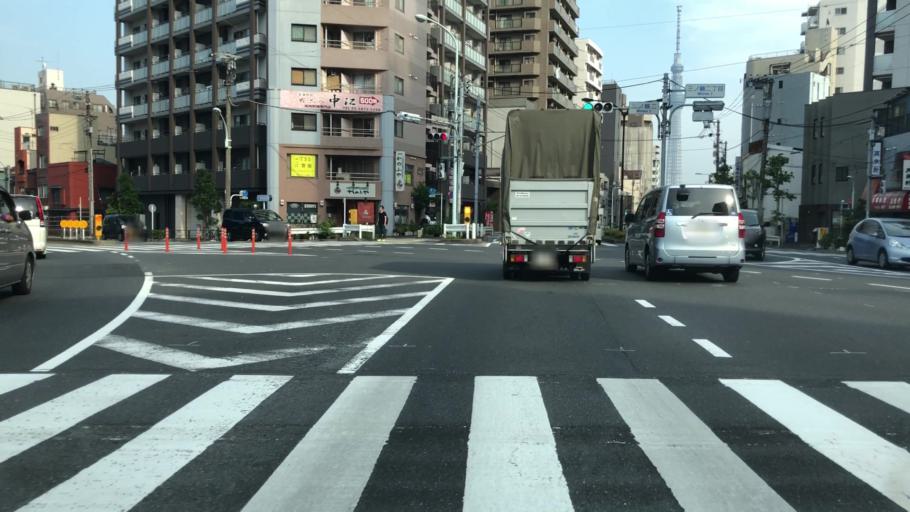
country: JP
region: Saitama
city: Soka
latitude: 35.7288
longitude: 139.7935
